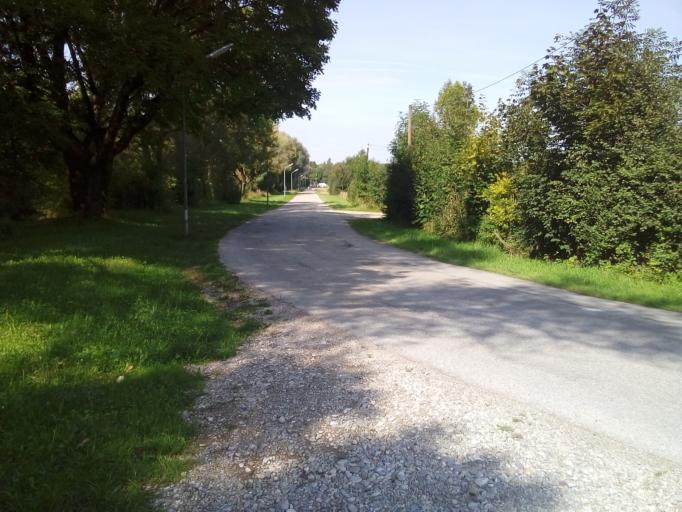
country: DE
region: Bavaria
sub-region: Upper Bavaria
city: Unterfoehring
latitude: 48.2008
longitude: 11.6559
